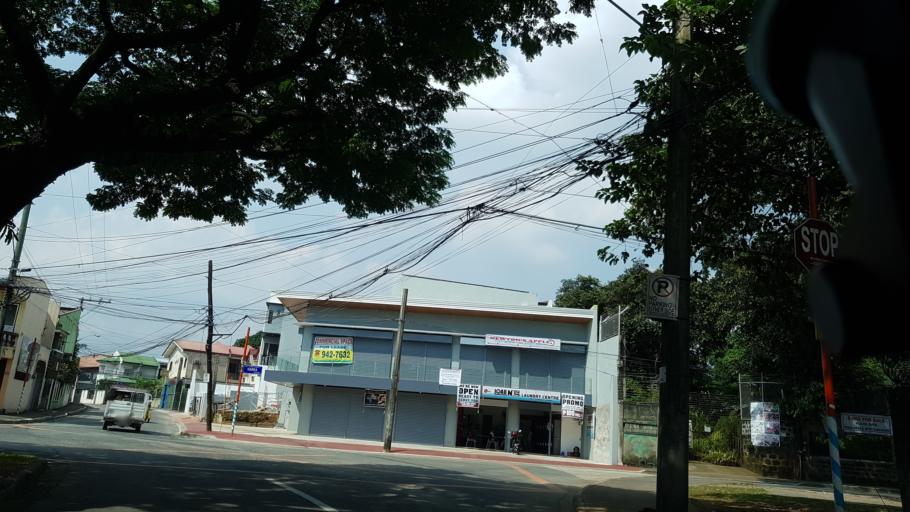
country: PH
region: Calabarzon
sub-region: Province of Rizal
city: Antipolo
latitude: 14.6538
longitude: 121.1162
